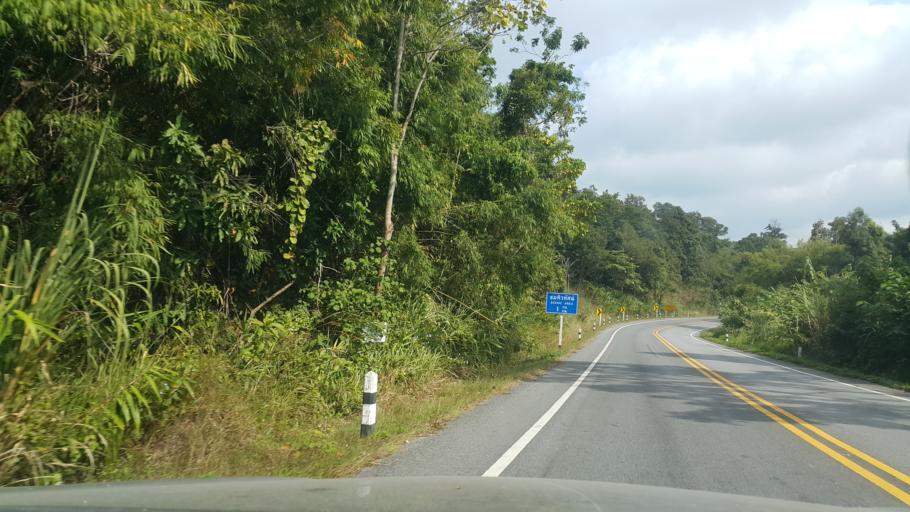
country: TH
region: Phayao
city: Phayao
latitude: 19.0618
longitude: 99.7752
